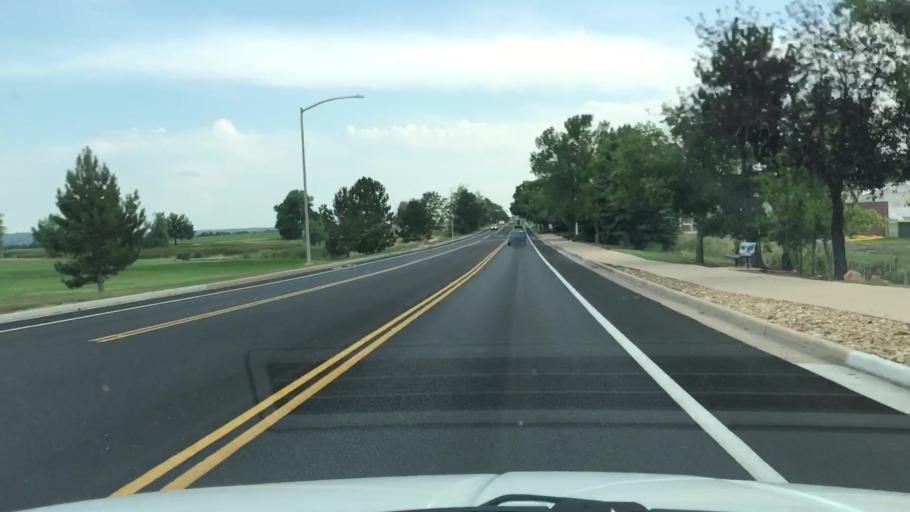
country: US
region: Colorado
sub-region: Broomfield County
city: Broomfield
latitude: 39.9322
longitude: -105.0720
